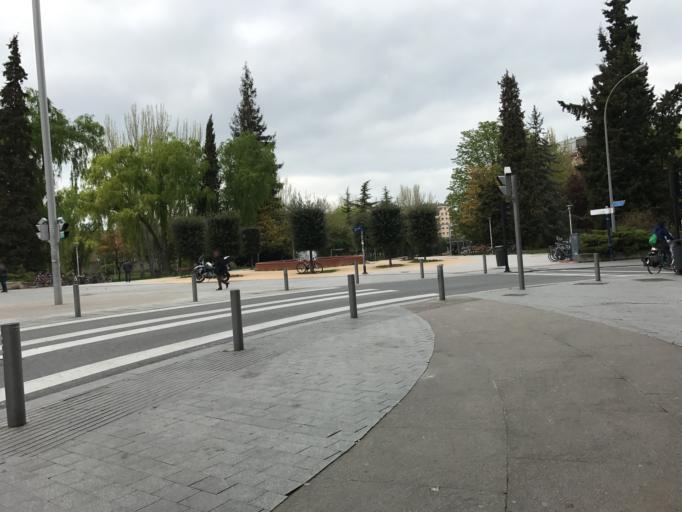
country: ES
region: Basque Country
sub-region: Provincia de Alava
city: Gasteiz / Vitoria
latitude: 42.8521
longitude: -2.6701
